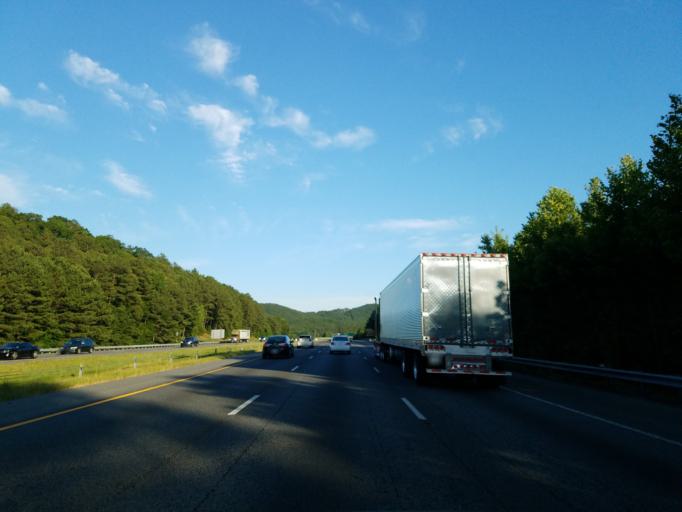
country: US
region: Georgia
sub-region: Bartow County
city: Emerson
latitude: 34.1504
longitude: -84.7459
